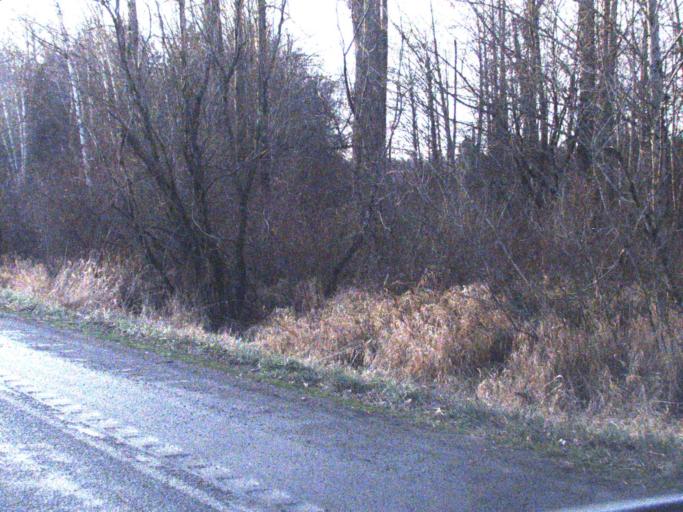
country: US
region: Washington
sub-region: Skagit County
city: Sedro-Woolley
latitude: 48.5187
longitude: -122.2046
